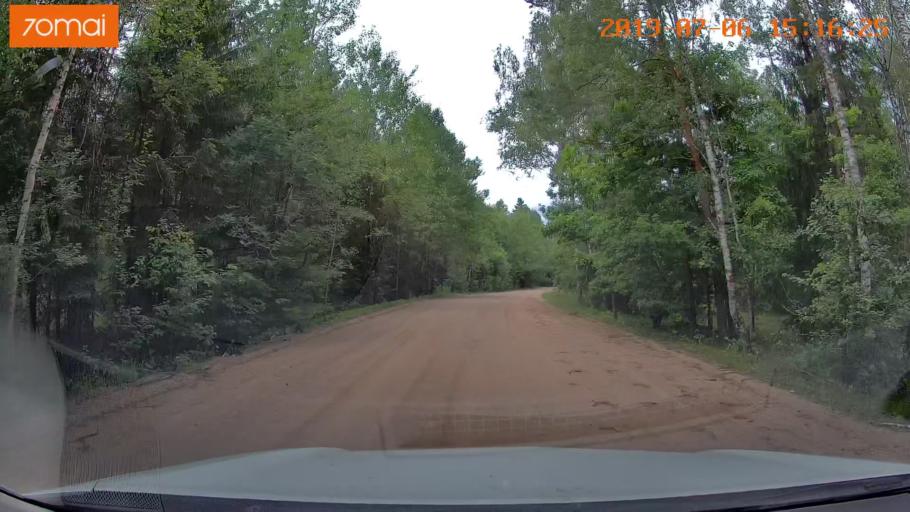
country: BY
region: Minsk
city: Ivyanyets
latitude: 53.9809
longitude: 26.6787
